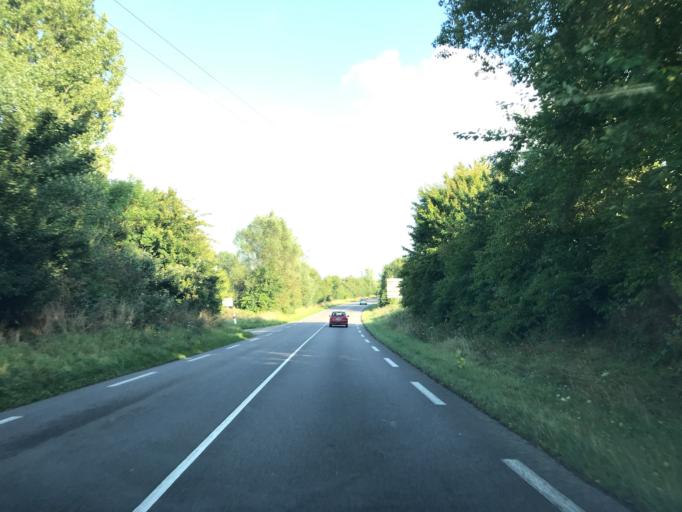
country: FR
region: Haute-Normandie
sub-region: Departement de la Seine-Maritime
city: Bolbec
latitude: 49.5798
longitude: 0.4511
